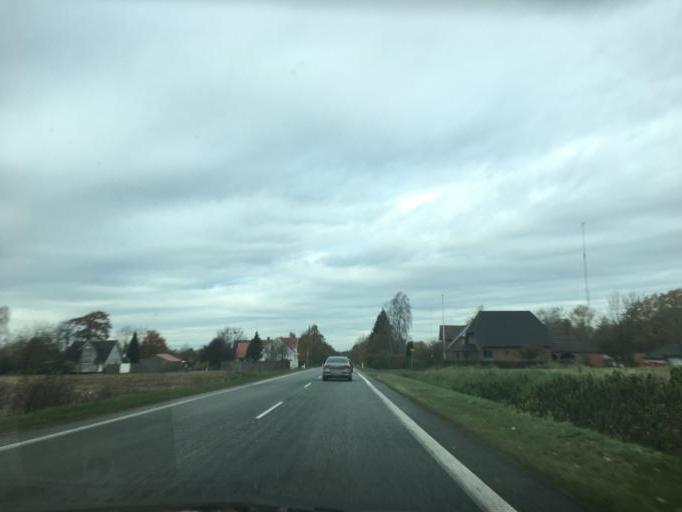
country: DK
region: South Denmark
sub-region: Vejle Kommune
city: Vejle
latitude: 55.6253
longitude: 9.4938
